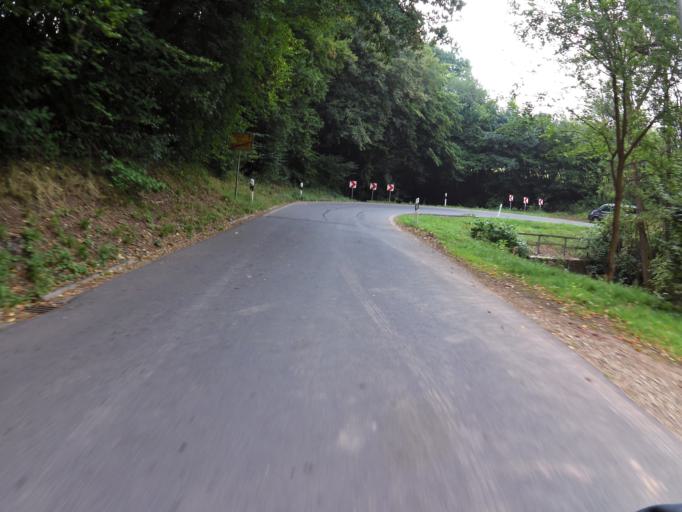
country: DE
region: Rheinland-Pfalz
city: Wilsecker
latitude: 50.0222
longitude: 6.5829
